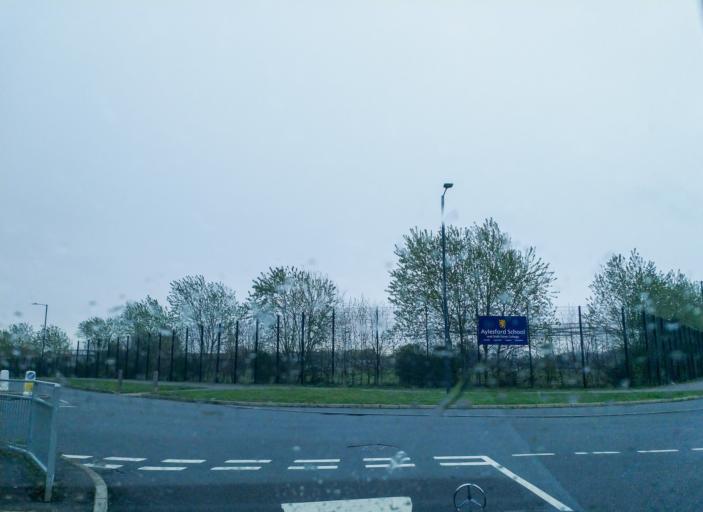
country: GB
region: England
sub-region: Warwickshire
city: Warwick
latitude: 52.2679
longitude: -1.6050
